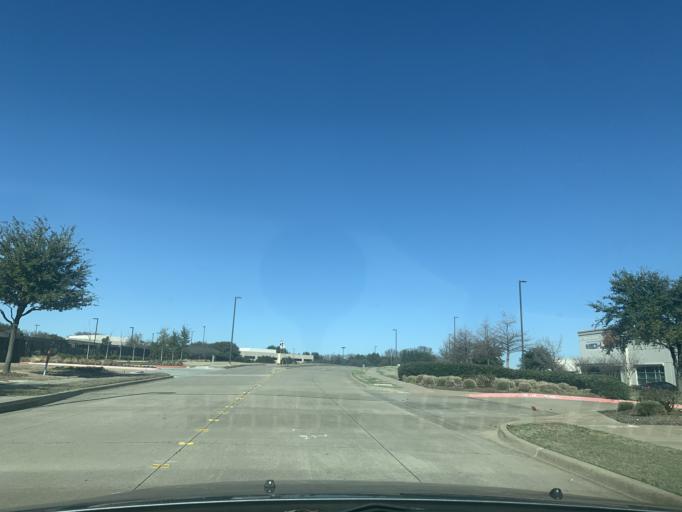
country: US
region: Texas
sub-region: Denton County
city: The Colony
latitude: 33.0658
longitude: -96.8093
